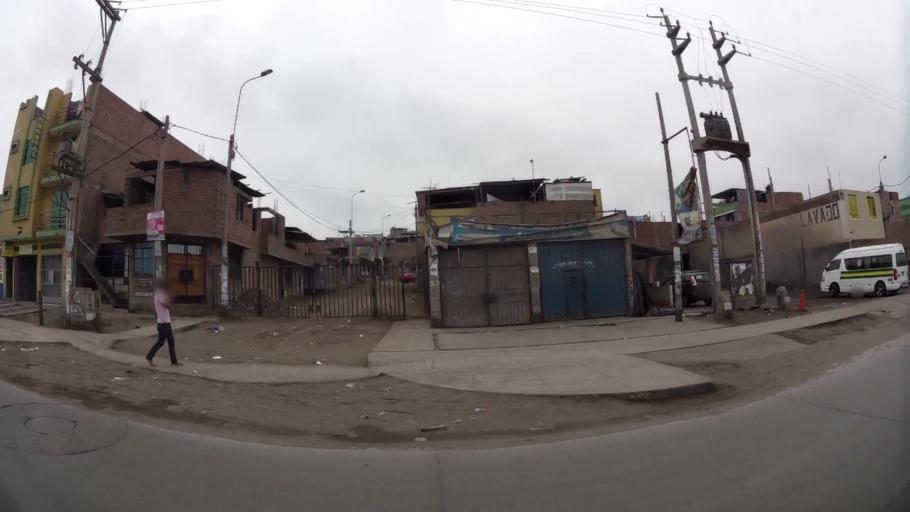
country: PE
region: Lima
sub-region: Lima
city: Surco
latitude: -12.2326
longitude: -76.9107
